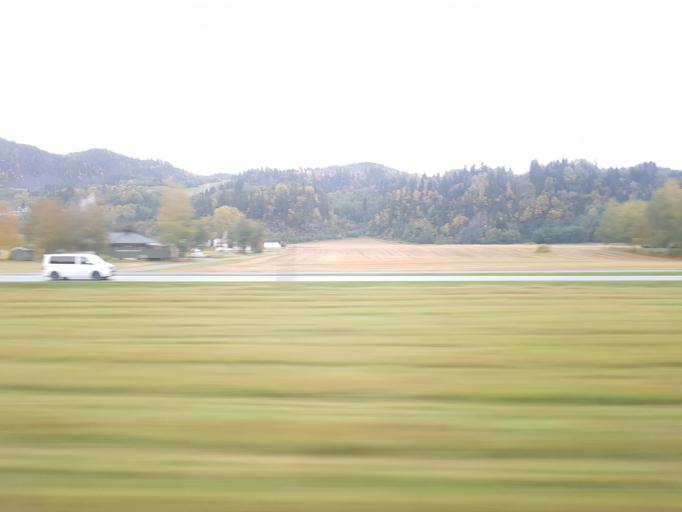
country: NO
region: Sor-Trondelag
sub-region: Melhus
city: Lundamo
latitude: 63.1264
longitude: 10.2471
